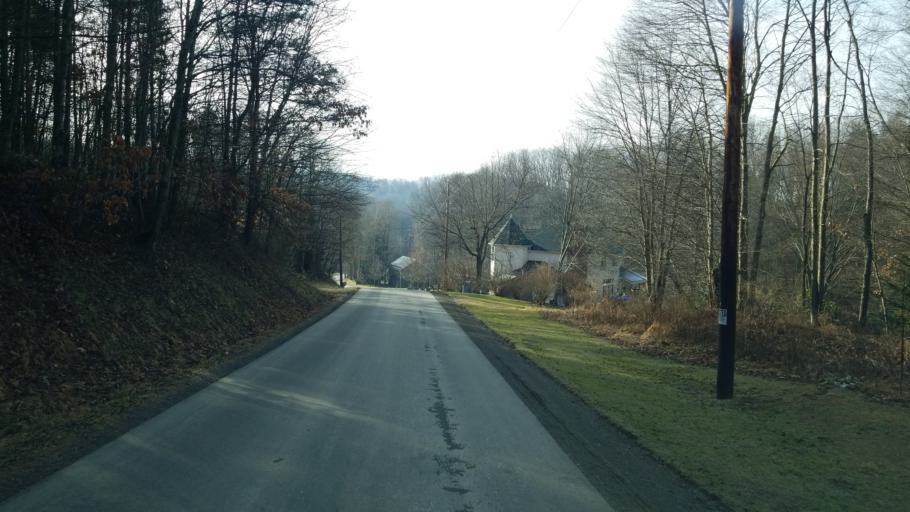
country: US
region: Pennsylvania
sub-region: Indiana County
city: Chevy Chase Heights
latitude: 40.8176
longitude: -79.1516
